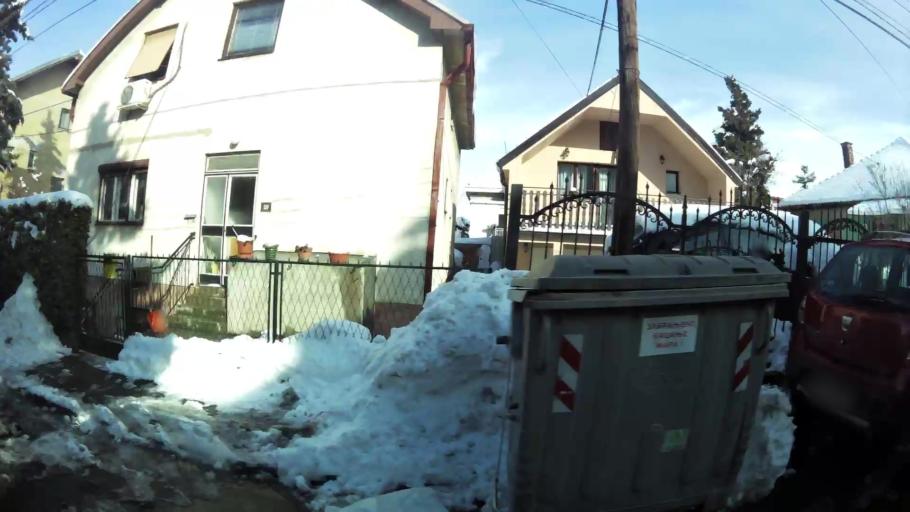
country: RS
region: Central Serbia
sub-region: Belgrade
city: Palilula
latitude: 44.8071
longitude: 20.5178
